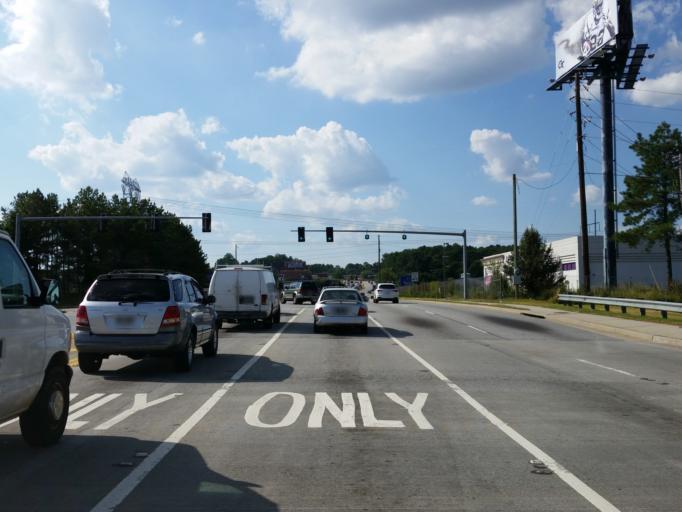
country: US
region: Georgia
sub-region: Gwinnett County
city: Duluth
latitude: 33.9487
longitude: -84.1378
